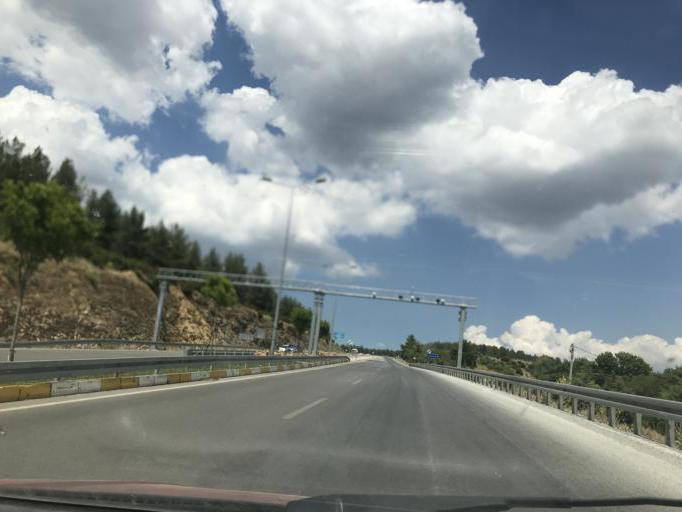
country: TR
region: Denizli
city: Tavas
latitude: 37.5759
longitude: 29.0865
